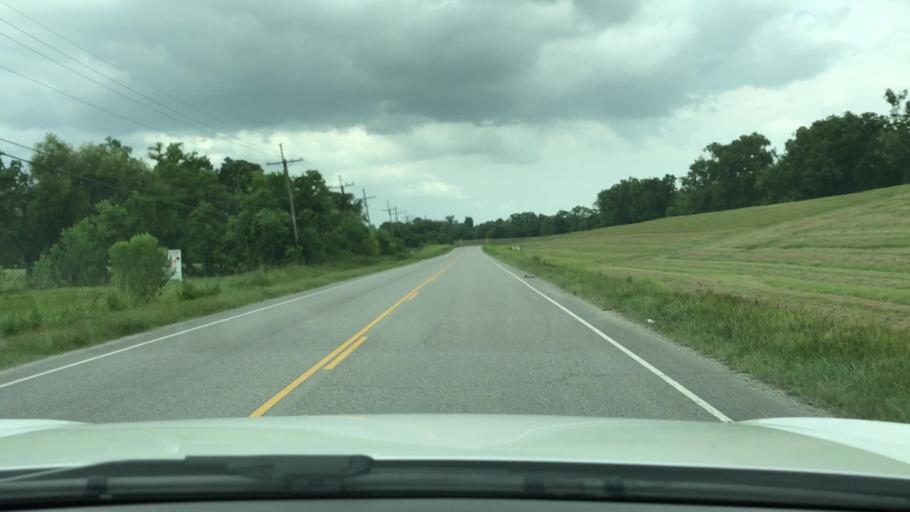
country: US
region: Louisiana
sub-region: Iberville Parish
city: Saint Gabriel
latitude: 30.2724
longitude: -91.1561
